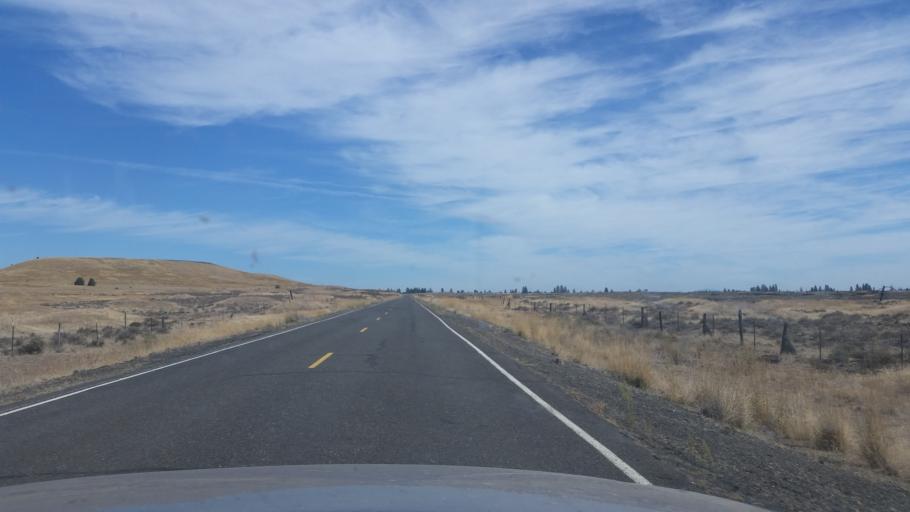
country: US
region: Washington
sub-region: Spokane County
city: Medical Lake
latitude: 47.3486
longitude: -117.8614
